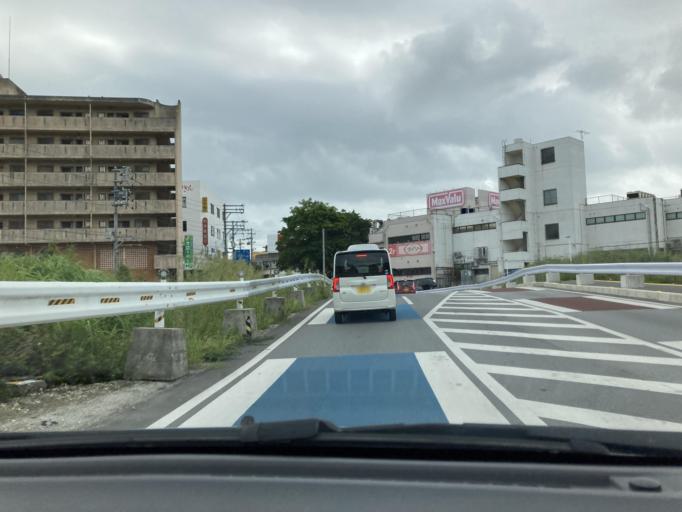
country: JP
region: Okinawa
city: Ginowan
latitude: 26.2398
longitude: 127.7491
